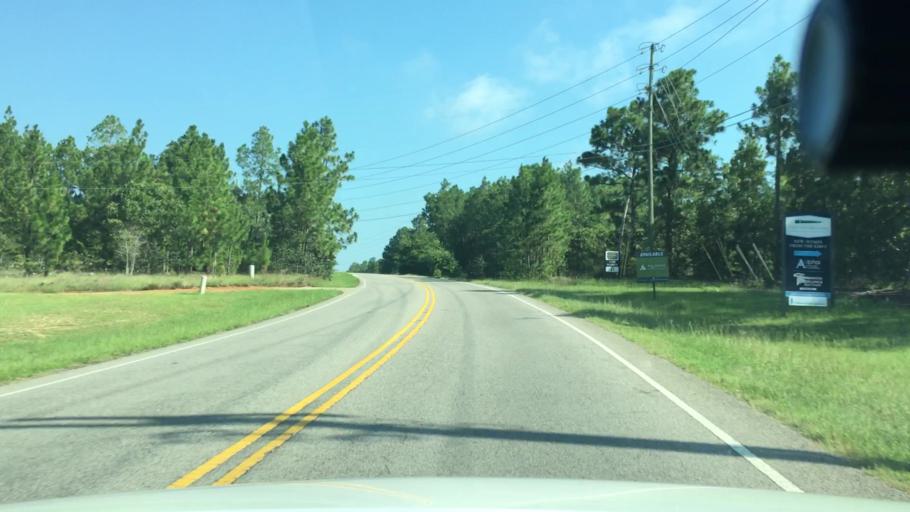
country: US
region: South Carolina
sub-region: Aiken County
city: Graniteville
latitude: 33.5916
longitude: -81.8367
